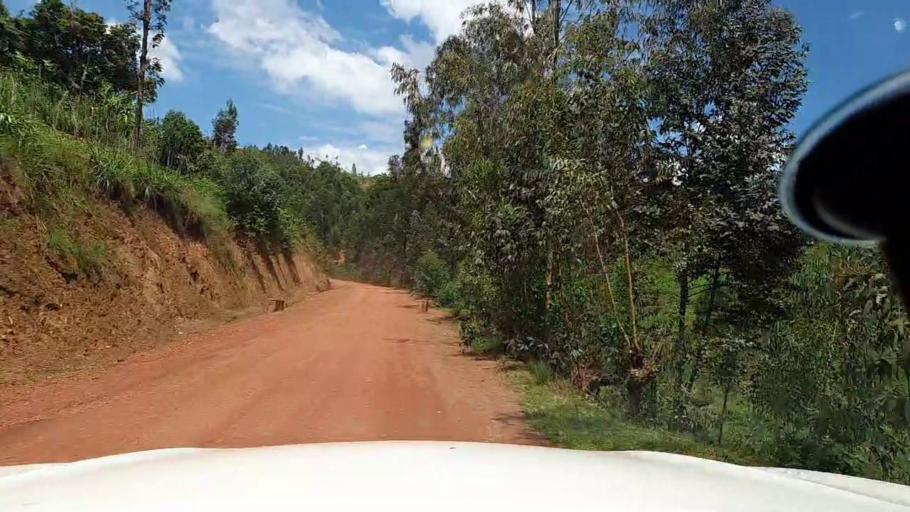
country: RW
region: Northern Province
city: Byumba
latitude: -1.7421
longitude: 29.8625
